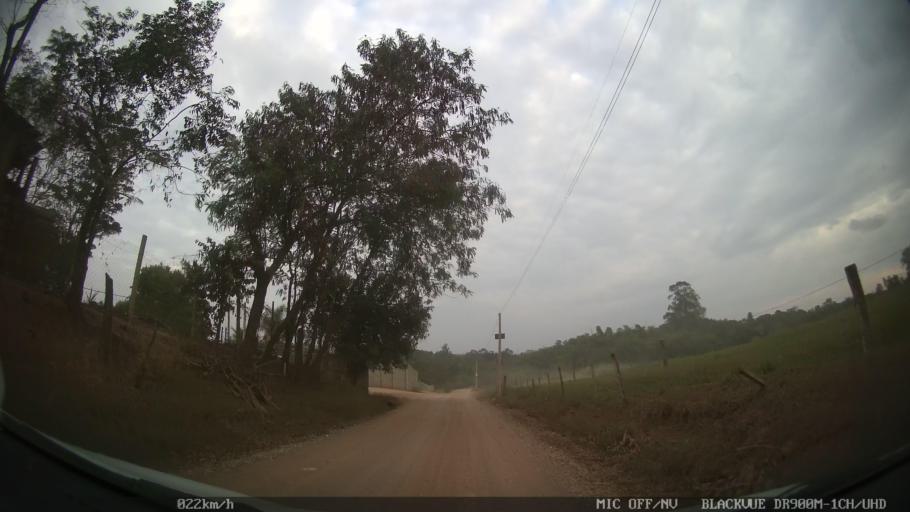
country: BR
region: Sao Paulo
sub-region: Santa Barbara D'Oeste
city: Santa Barbara d'Oeste
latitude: -22.6933
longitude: -47.3875
